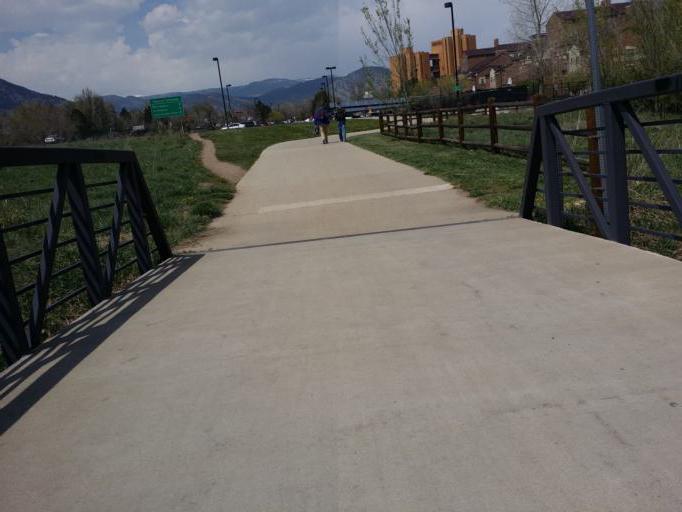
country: US
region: Colorado
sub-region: Boulder County
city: Boulder
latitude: 39.9950
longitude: -105.2487
